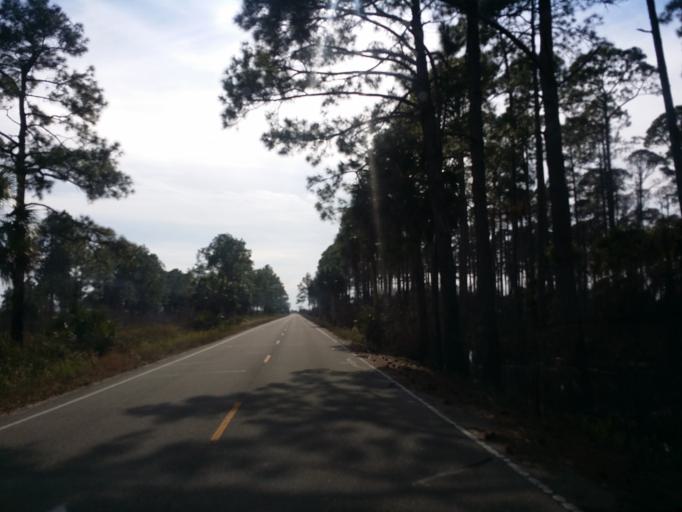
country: US
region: Florida
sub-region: Leon County
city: Woodville
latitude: 30.1397
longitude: -84.1396
